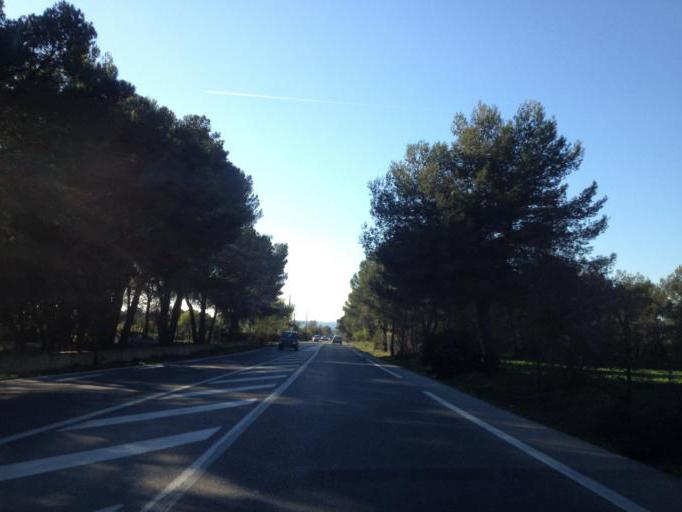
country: FR
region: Provence-Alpes-Cote d'Azur
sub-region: Departement des Bouches-du-Rhone
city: Eguilles
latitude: 43.6031
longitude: 5.3414
